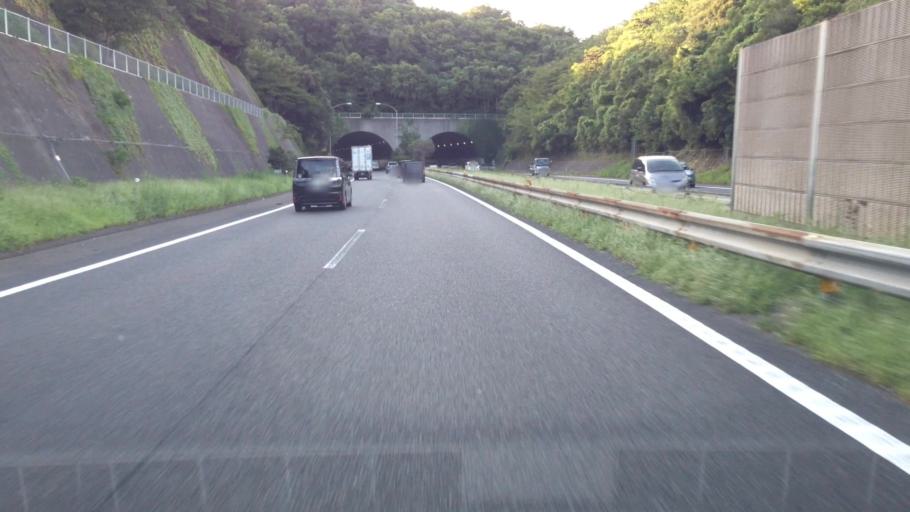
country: JP
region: Kanagawa
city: Zushi
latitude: 35.3214
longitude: 139.6037
